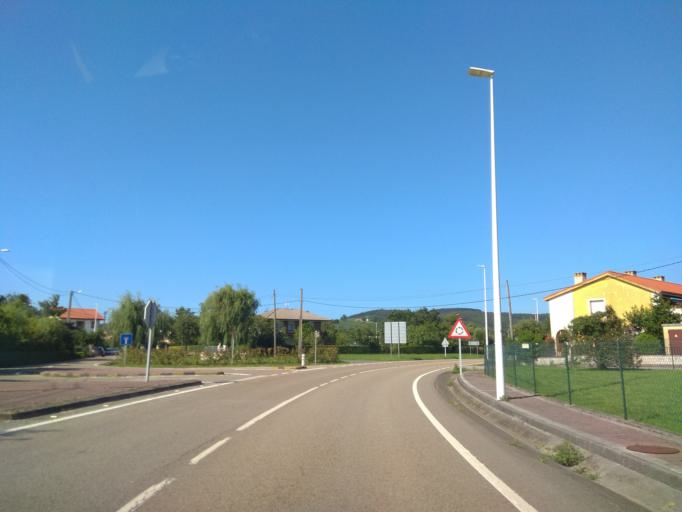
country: ES
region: Cantabria
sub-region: Provincia de Cantabria
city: Bareyo
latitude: 43.4642
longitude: -3.6731
